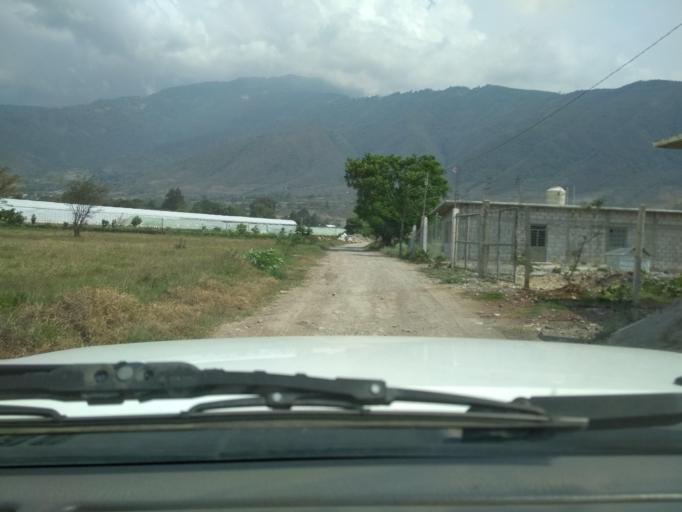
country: MX
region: Veracruz
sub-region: Acultzingo
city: Sierra de Agua
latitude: 18.7585
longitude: -97.2297
